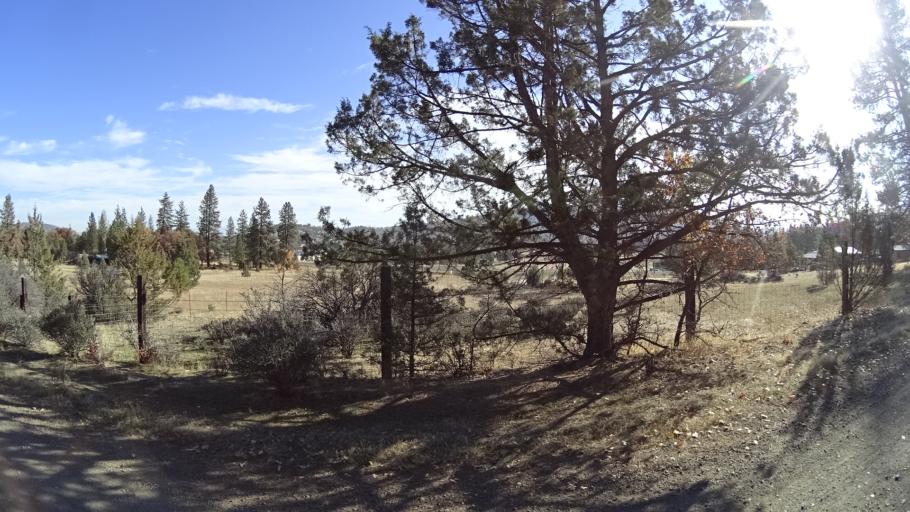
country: US
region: California
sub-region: Siskiyou County
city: Yreka
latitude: 41.6970
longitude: -122.6510
